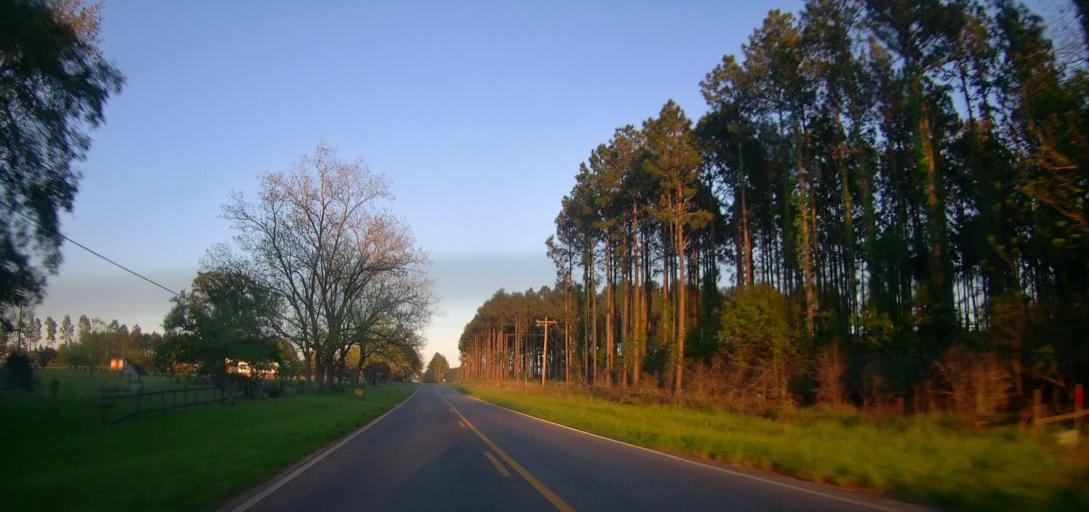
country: US
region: Georgia
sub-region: Ben Hill County
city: Fitzgerald
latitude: 31.7178
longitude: -83.2949
